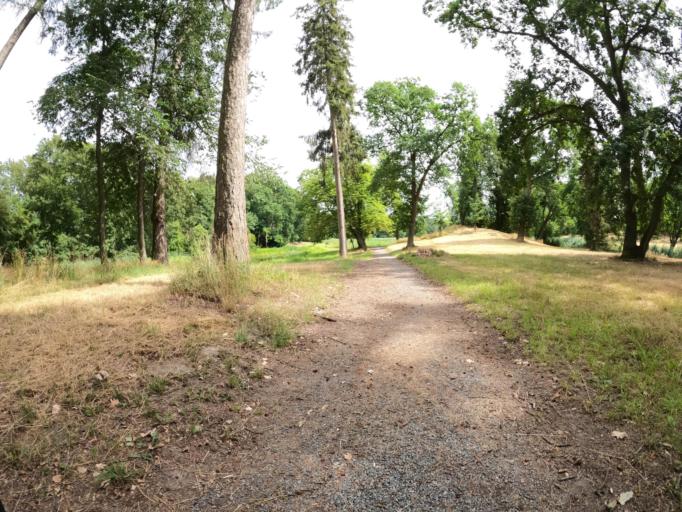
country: DE
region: Mecklenburg-Vorpommern
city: Loitz
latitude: 53.4058
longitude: 13.4458
